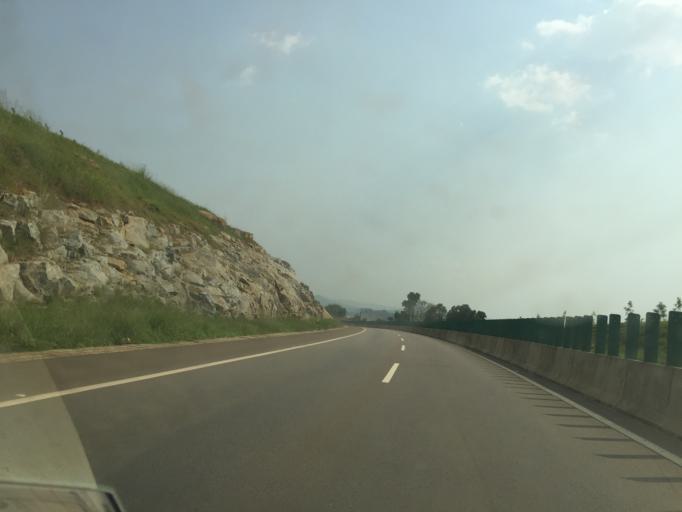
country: UG
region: Central Region
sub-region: Wakiso District
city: Kajansi
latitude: 0.2630
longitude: 32.5205
